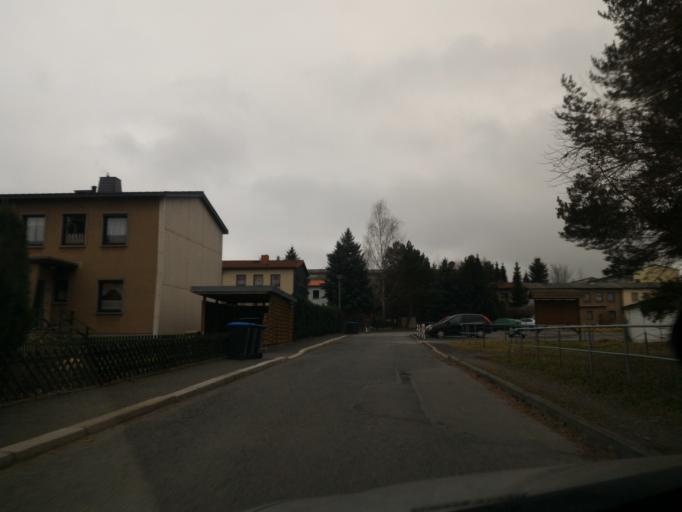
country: DE
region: Saxony
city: Grossschonau
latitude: 50.8905
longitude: 14.6664
